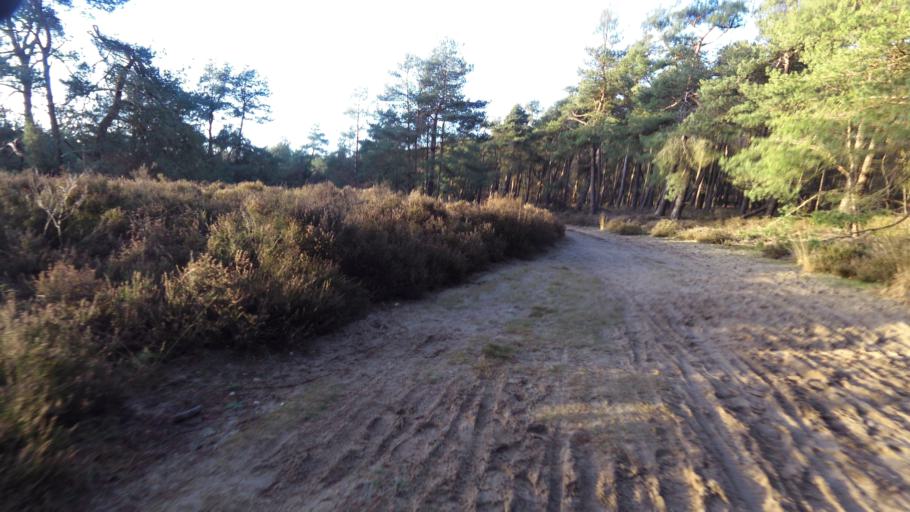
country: NL
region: Gelderland
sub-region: Gemeente Apeldoorn
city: Uddel
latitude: 52.2161
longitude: 5.8609
